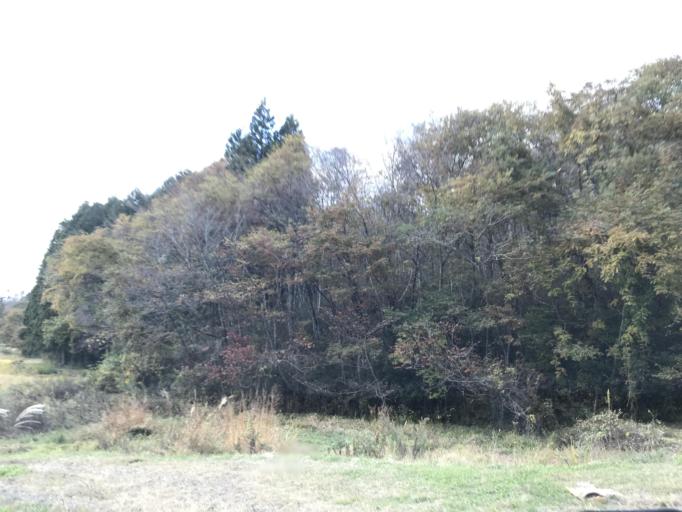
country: JP
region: Iwate
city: Ichinoseki
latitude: 38.8766
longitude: 141.1298
